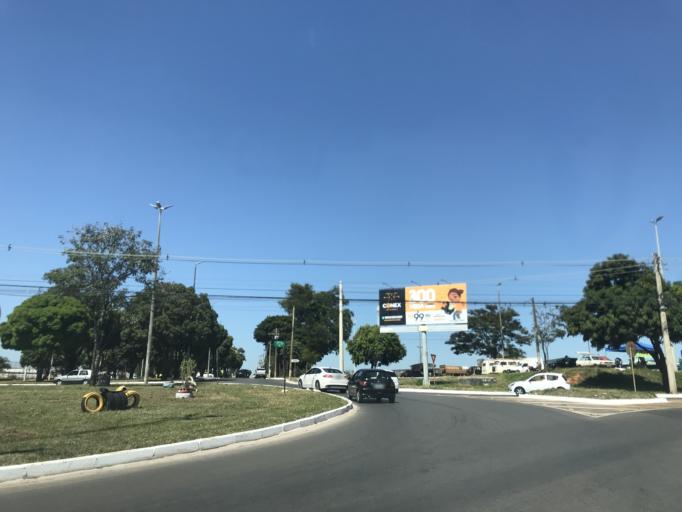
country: BR
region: Federal District
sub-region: Brasilia
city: Brasilia
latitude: -15.6499
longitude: -47.7852
